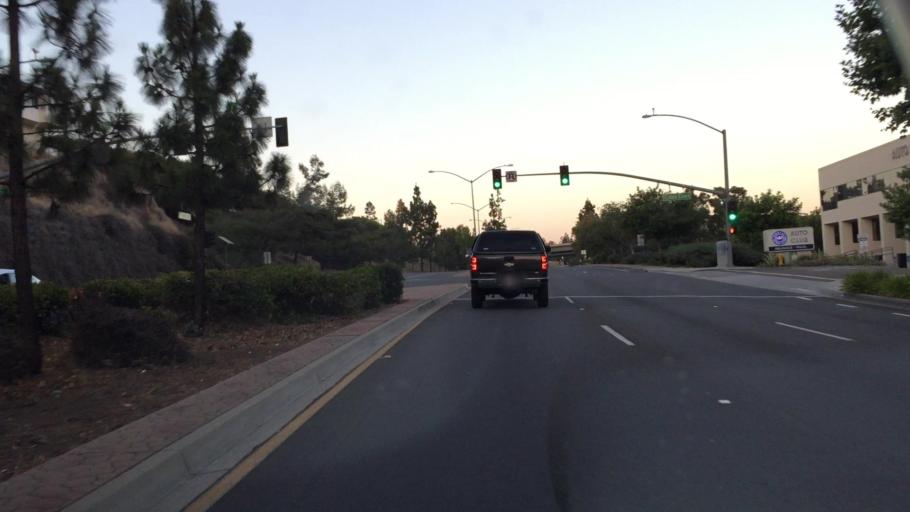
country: US
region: California
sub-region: San Diego County
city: La Mesa
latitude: 32.7834
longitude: -117.0104
